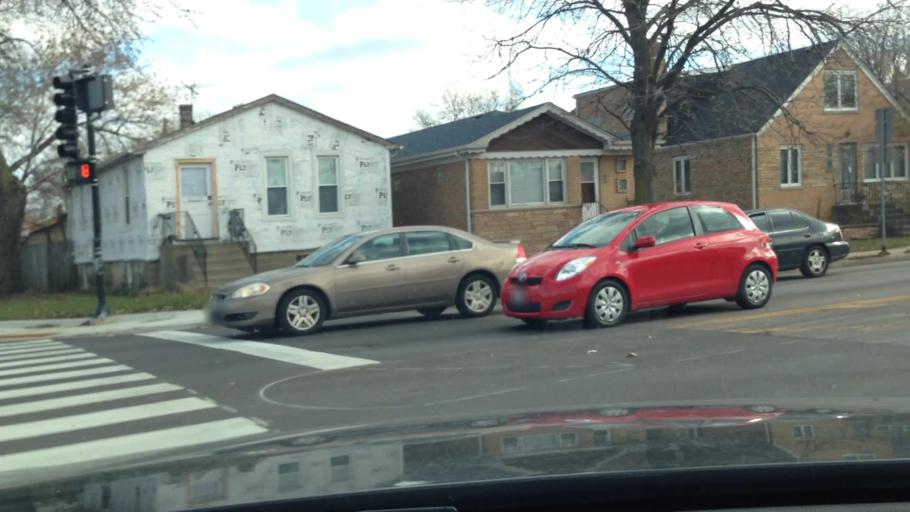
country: US
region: Illinois
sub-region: Cook County
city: Harwood Heights
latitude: 41.9820
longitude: -87.7878
